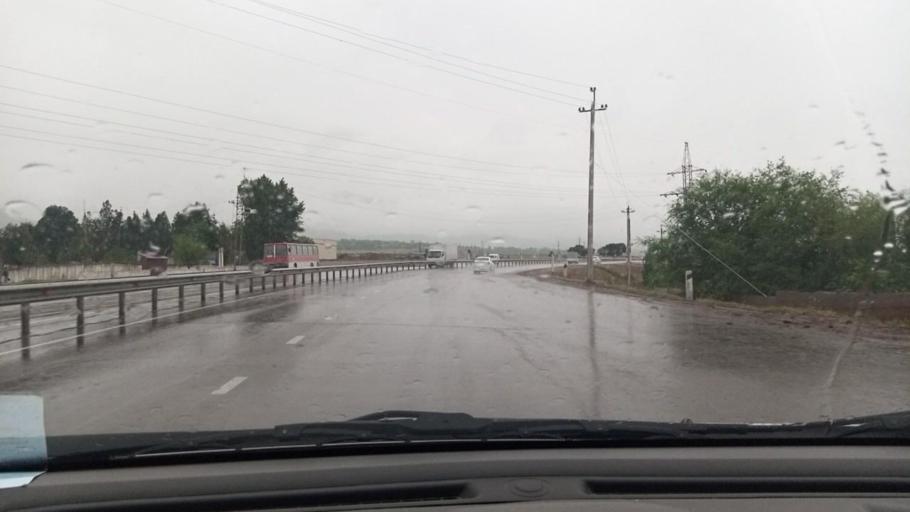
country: UZ
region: Toshkent
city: Angren
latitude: 41.0303
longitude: 70.1376
